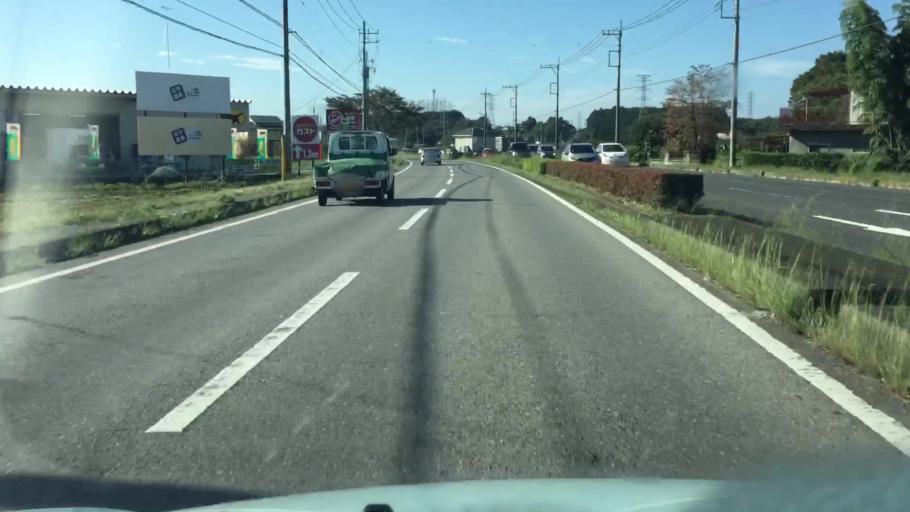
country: JP
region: Tochigi
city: Ujiie
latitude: 36.6341
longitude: 139.9949
